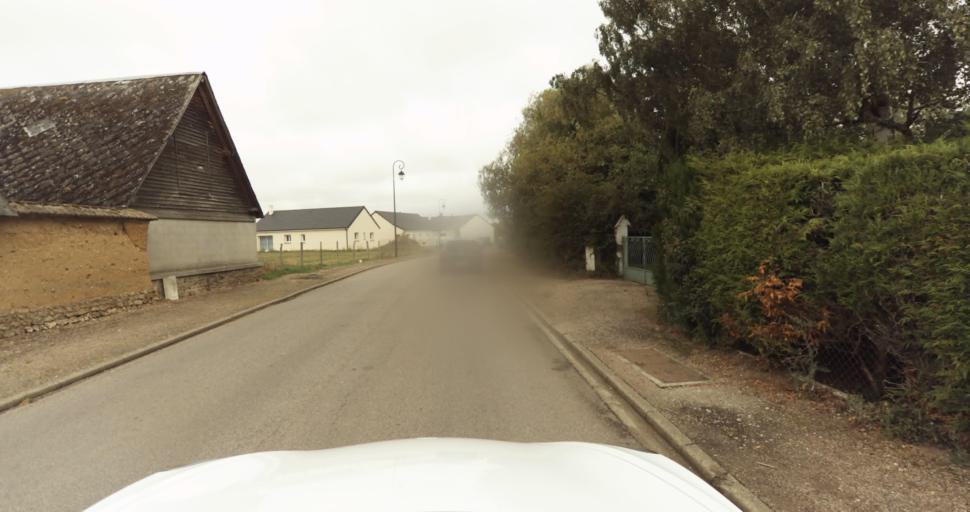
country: FR
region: Haute-Normandie
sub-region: Departement de l'Eure
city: Aviron
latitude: 49.0491
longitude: 1.0859
